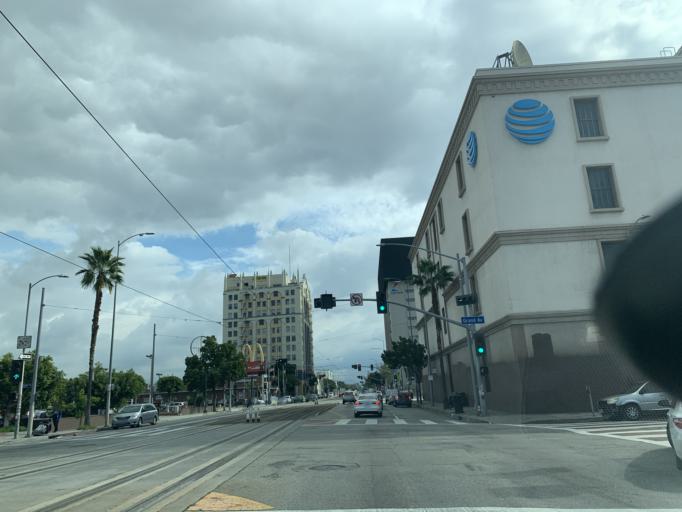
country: US
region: California
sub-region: Los Angeles County
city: Los Angeles
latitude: 34.0327
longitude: -118.2686
